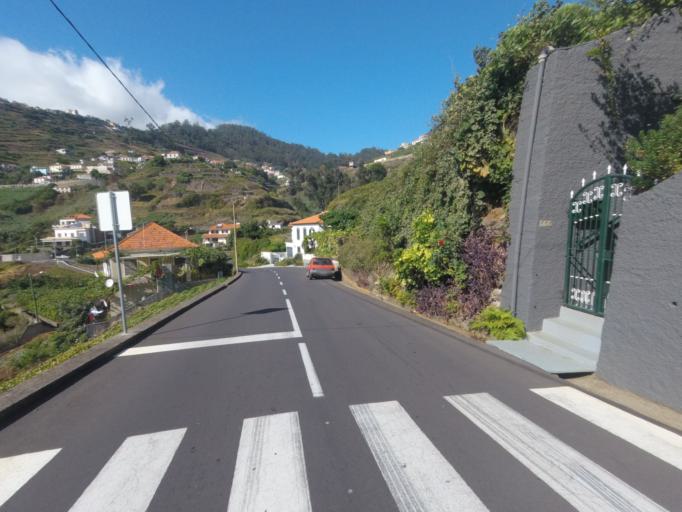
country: PT
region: Madeira
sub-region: Ribeira Brava
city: Campanario
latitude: 32.6739
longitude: -17.0240
